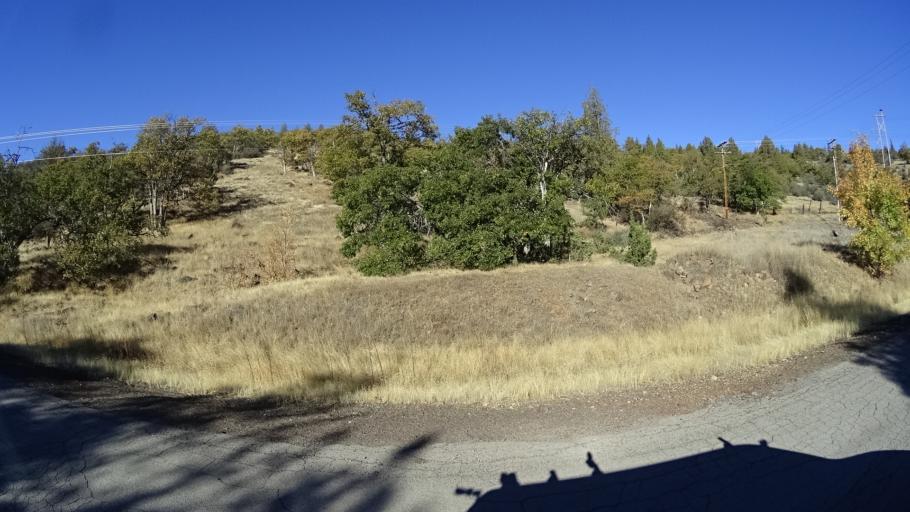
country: US
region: California
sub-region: Siskiyou County
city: Montague
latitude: 41.9767
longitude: -122.3646
